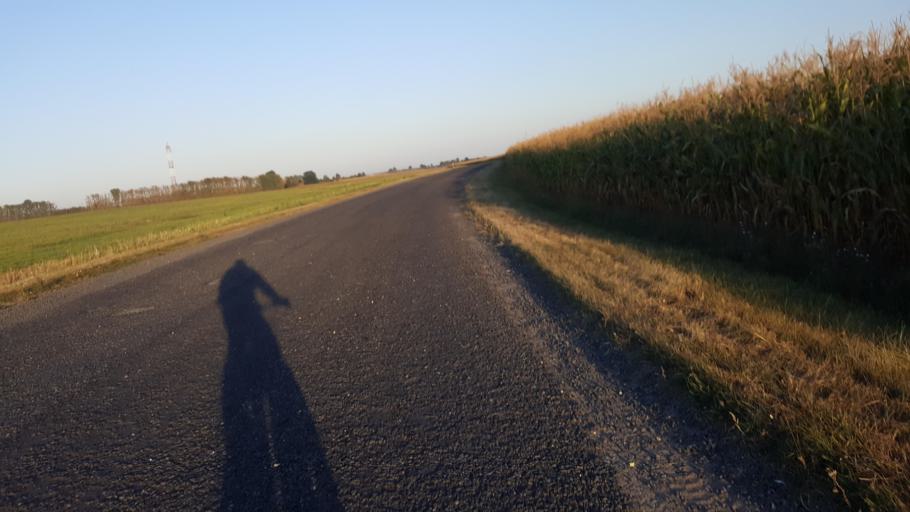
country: BY
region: Brest
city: Vysokaye
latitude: 52.2987
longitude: 23.4992
